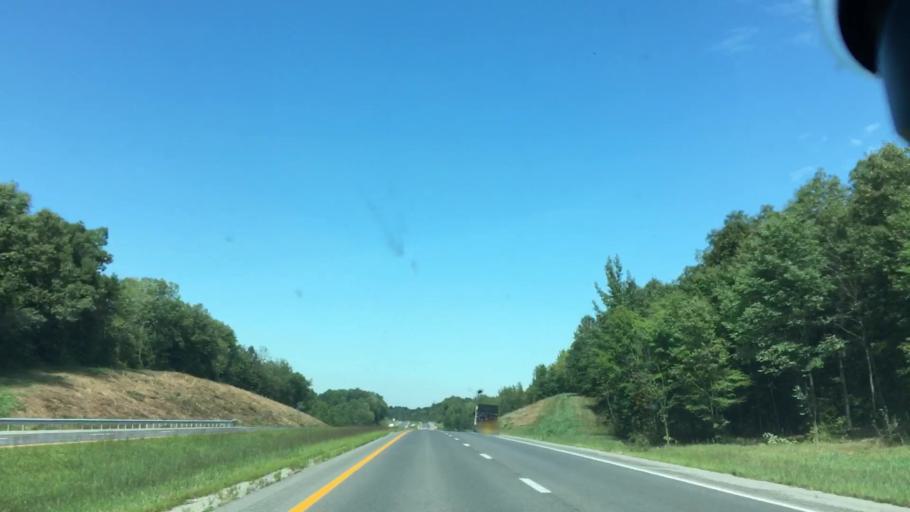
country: US
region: Kentucky
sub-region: Webster County
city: Sebree
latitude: 37.5201
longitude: -87.4750
